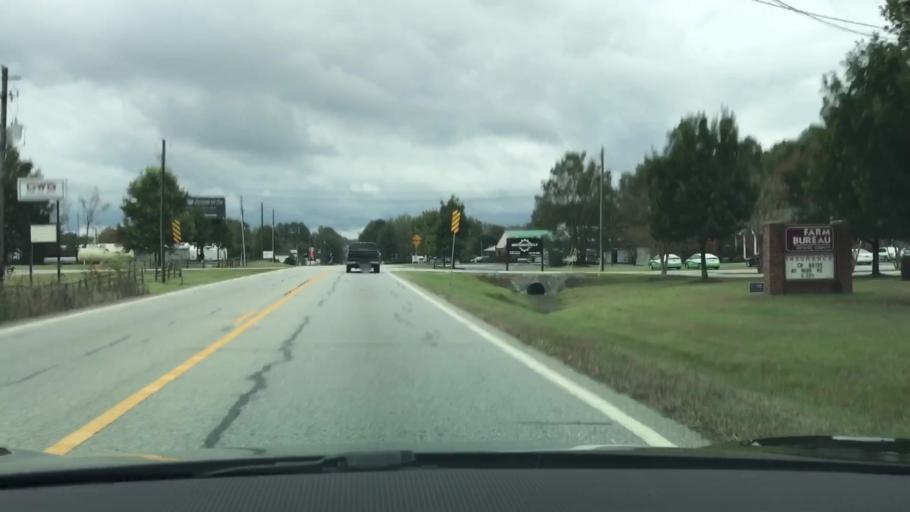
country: US
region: Georgia
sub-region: Oconee County
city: Watkinsville
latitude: 33.8542
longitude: -83.4001
